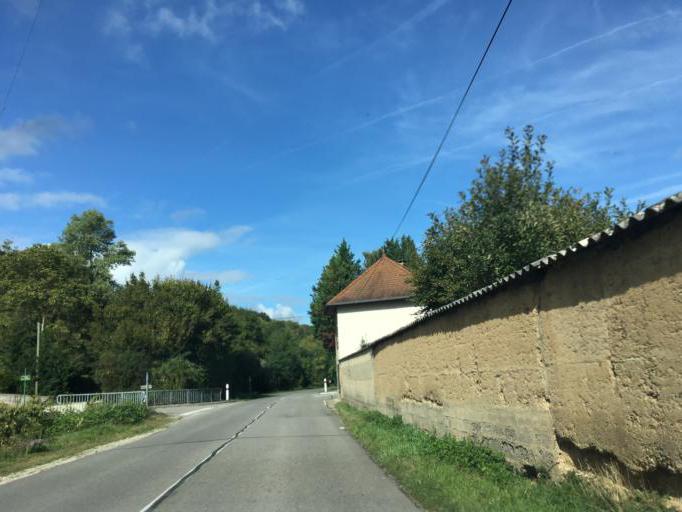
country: FR
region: Rhone-Alpes
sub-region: Departement de l'Isere
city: Saint-Clair-de-la-Tour
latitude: 45.5647
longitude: 5.4762
